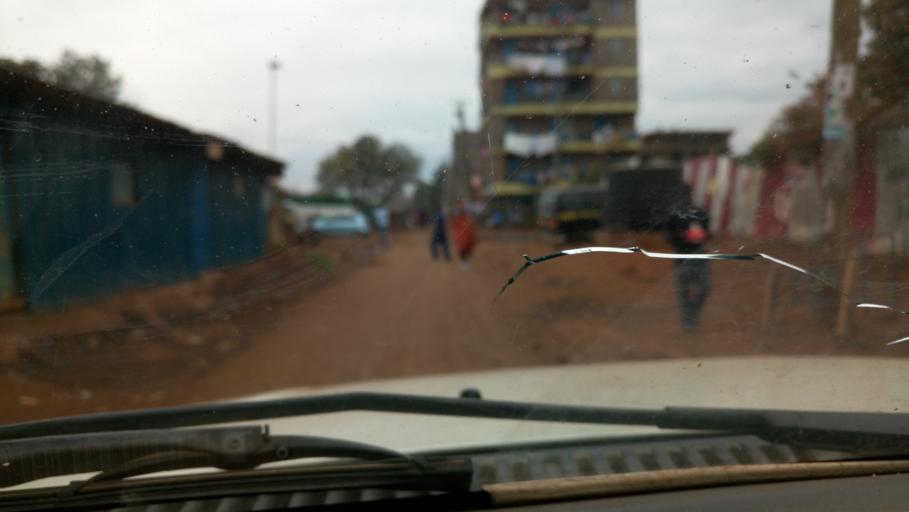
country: KE
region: Nairobi Area
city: Pumwani
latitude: -1.2467
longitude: 36.8853
